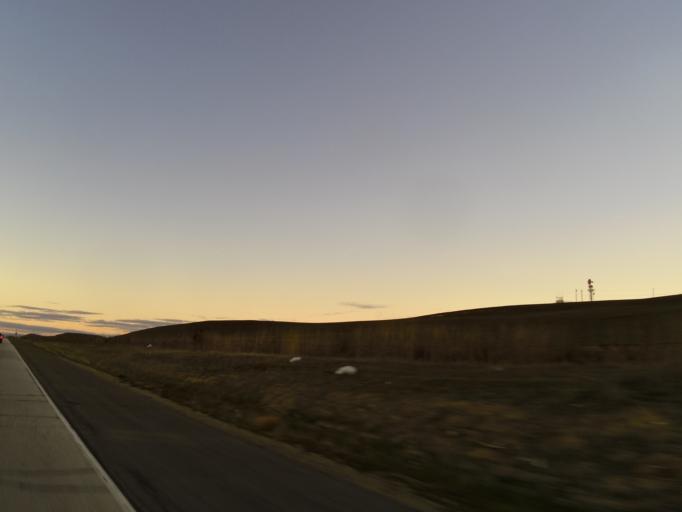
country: US
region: California
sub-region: Monterey County
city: King City
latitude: 36.1325
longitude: -121.0304
